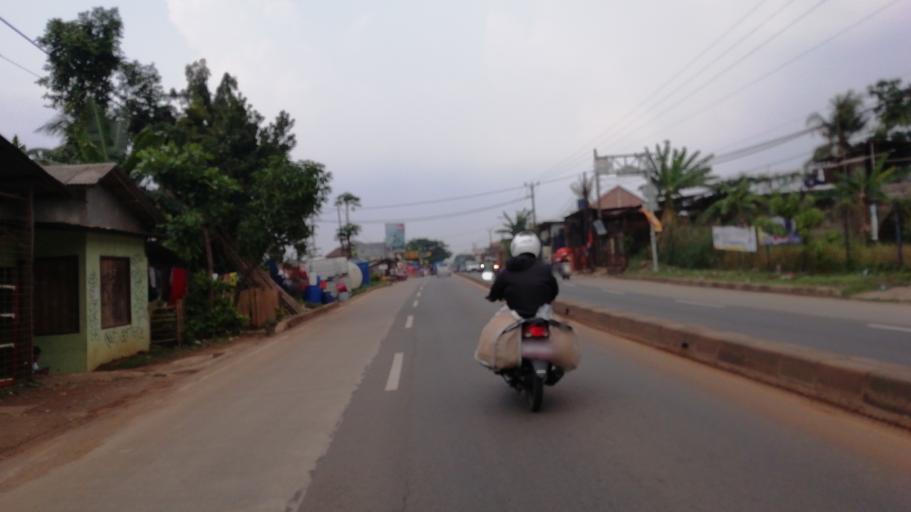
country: ID
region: West Java
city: Parung
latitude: -6.4653
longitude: 106.7292
